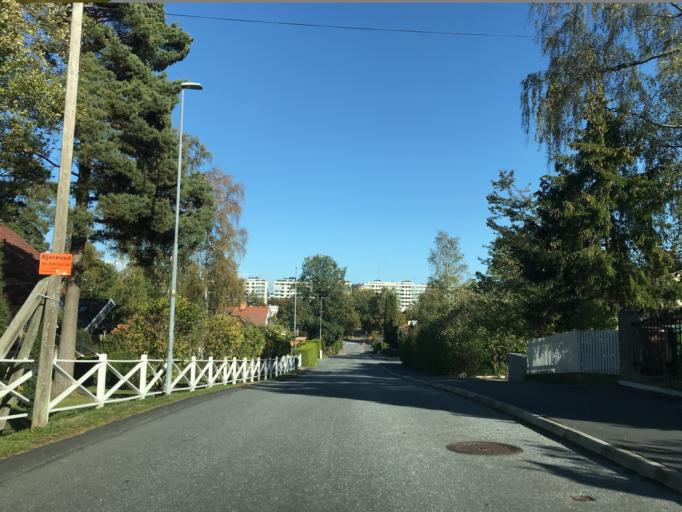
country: SE
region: Stockholm
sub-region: Sollentuna Kommun
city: Sollentuna
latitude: 59.4242
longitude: 17.9397
